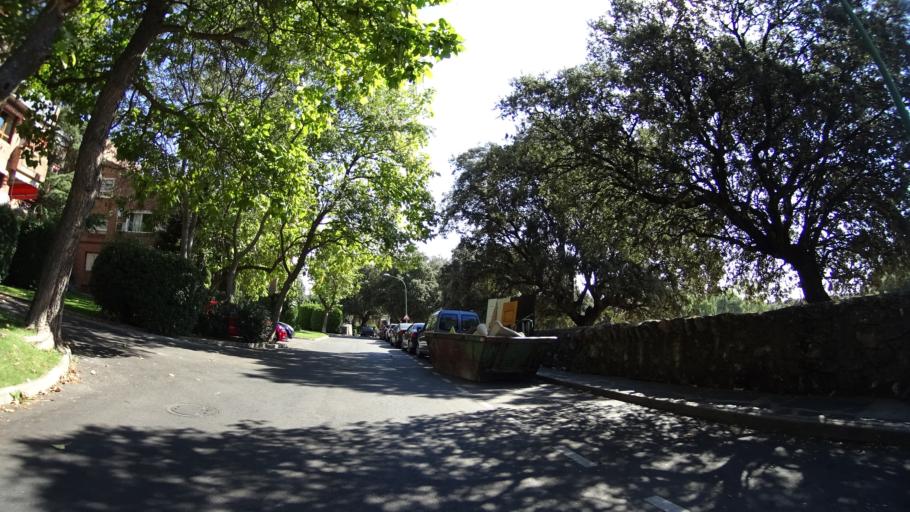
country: ES
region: Madrid
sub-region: Provincia de Madrid
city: Navalquejigo
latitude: 40.6067
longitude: -4.0278
